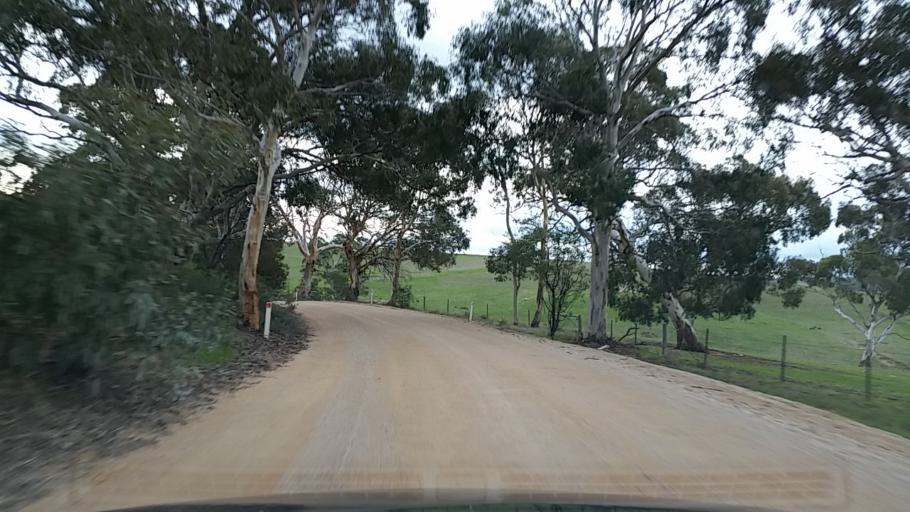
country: AU
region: South Australia
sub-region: Mount Barker
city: Nairne
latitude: -34.9603
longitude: 139.0225
